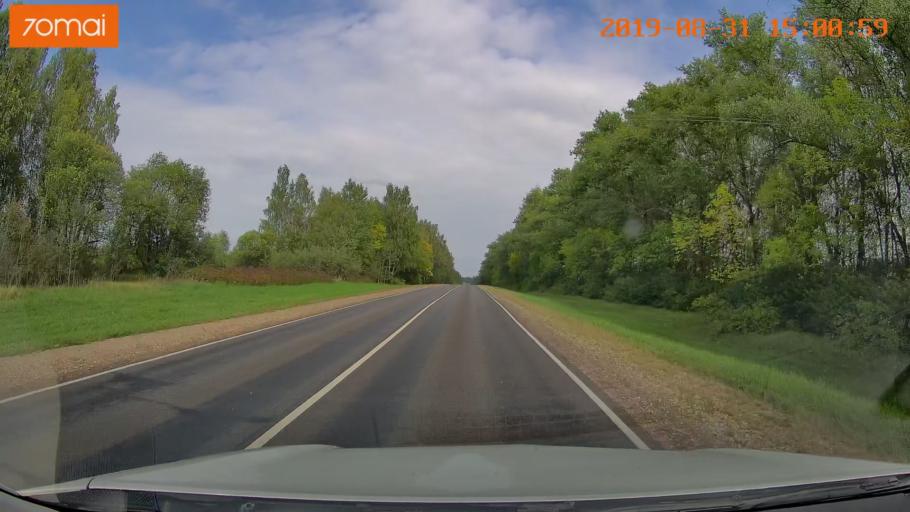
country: RU
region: Kaluga
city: Spas-Demensk
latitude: 54.3361
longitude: 34.0453
